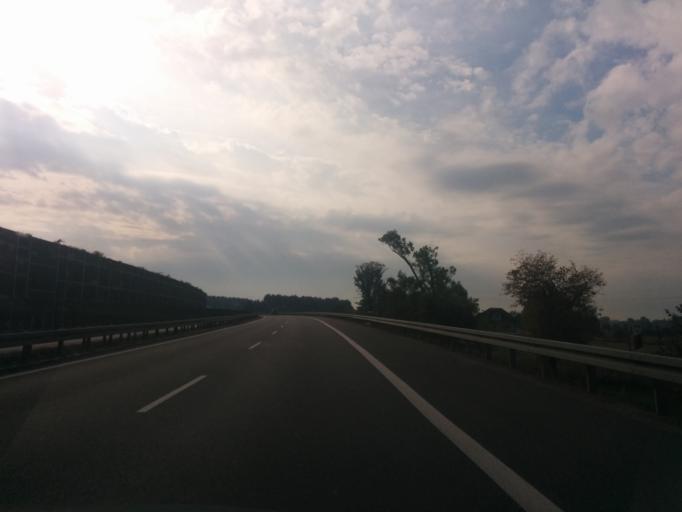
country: PL
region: Masovian Voivodeship
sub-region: Powiat bialobrzeski
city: Stara Blotnica
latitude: 51.5816
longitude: 21.0014
